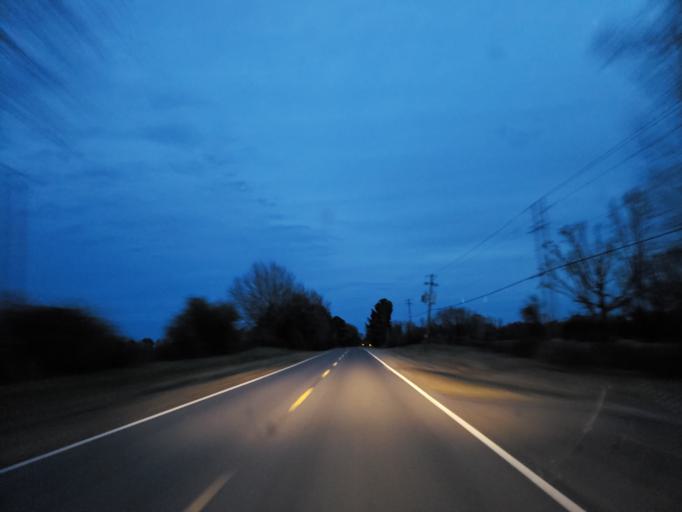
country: US
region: Alabama
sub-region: Greene County
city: Eutaw
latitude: 32.8903
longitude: -87.9483
